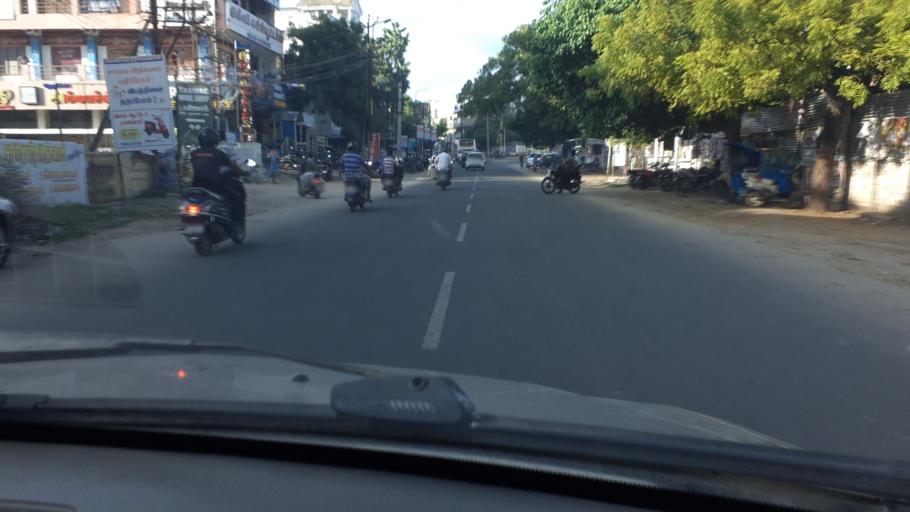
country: IN
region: Tamil Nadu
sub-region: Tirunelveli Kattabo
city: Tirunelveli
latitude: 8.7234
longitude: 77.7319
